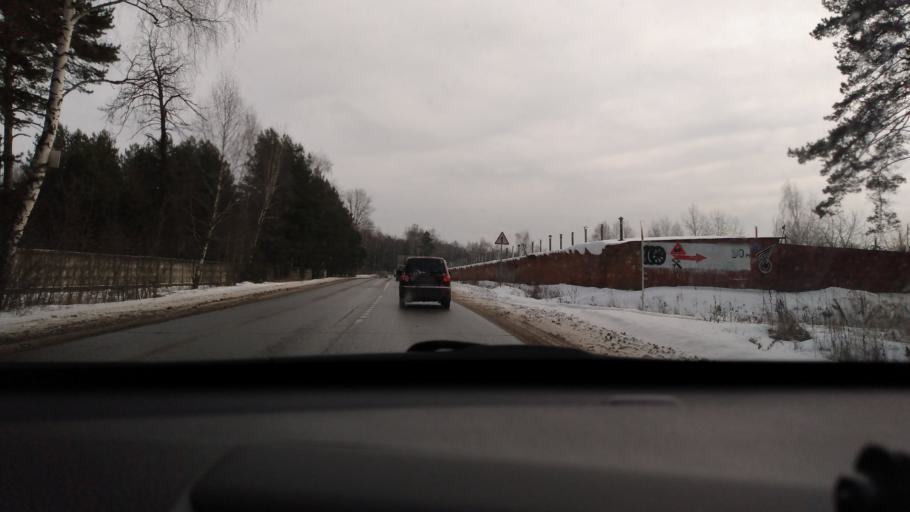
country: RU
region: Moskovskaya
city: Chornaya
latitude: 55.7658
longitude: 38.0669
